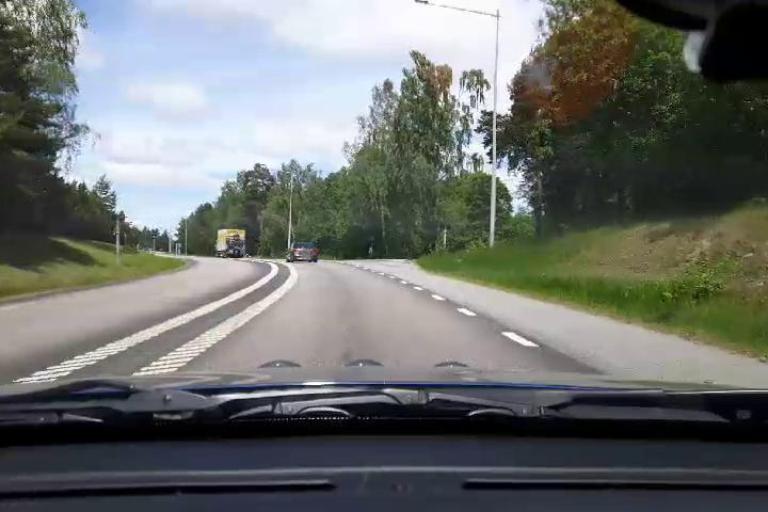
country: SE
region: Uppsala
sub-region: Osthammars Kommun
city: Bjorklinge
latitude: 60.0281
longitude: 17.5536
